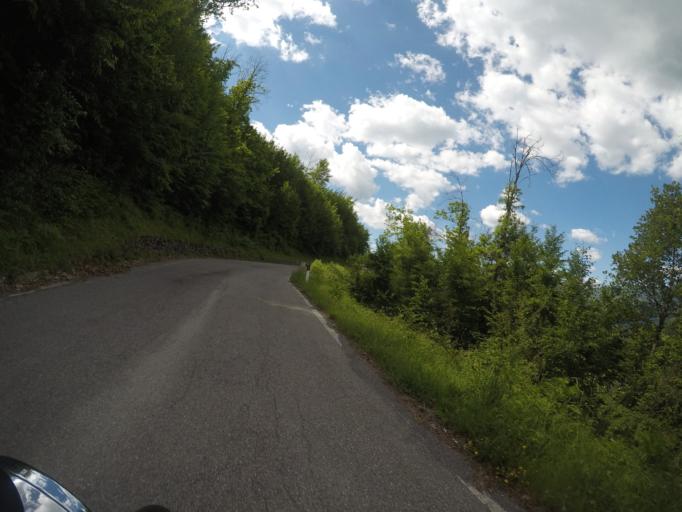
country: IT
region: Tuscany
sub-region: Provincia di Lucca
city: Minucciano
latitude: 44.1680
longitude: 10.2013
